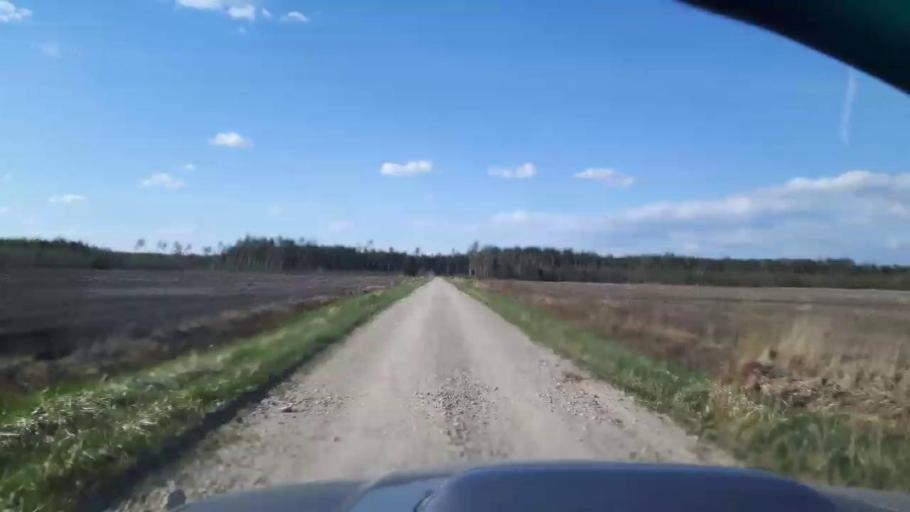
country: EE
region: Paernumaa
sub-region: Tootsi vald
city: Tootsi
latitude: 58.4175
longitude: 24.8526
